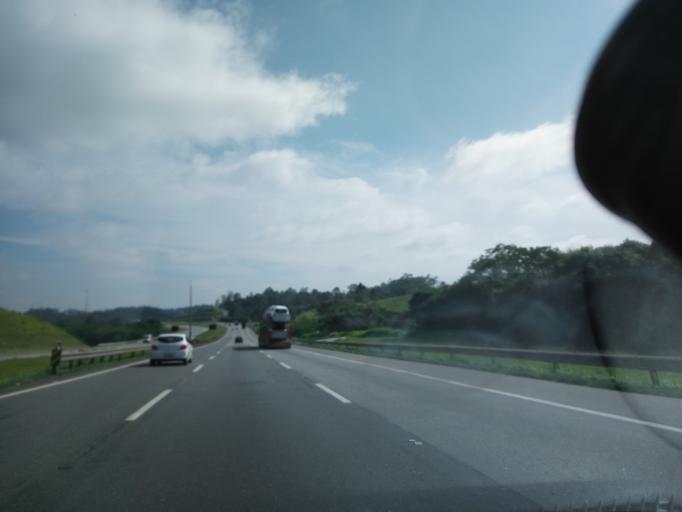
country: BR
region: Sao Paulo
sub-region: Itapecerica Da Serra
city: Itapecerica da Serra
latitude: -23.7327
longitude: -46.8107
